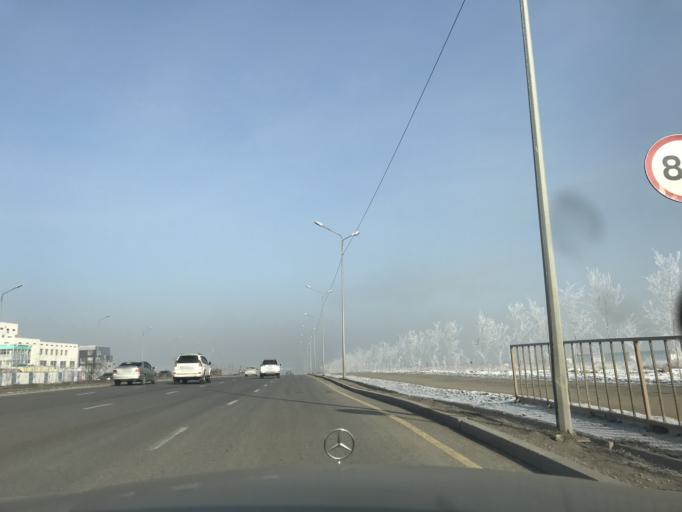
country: KZ
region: Almaty Oblysy
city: Burunday
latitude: 43.3154
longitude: 76.8342
